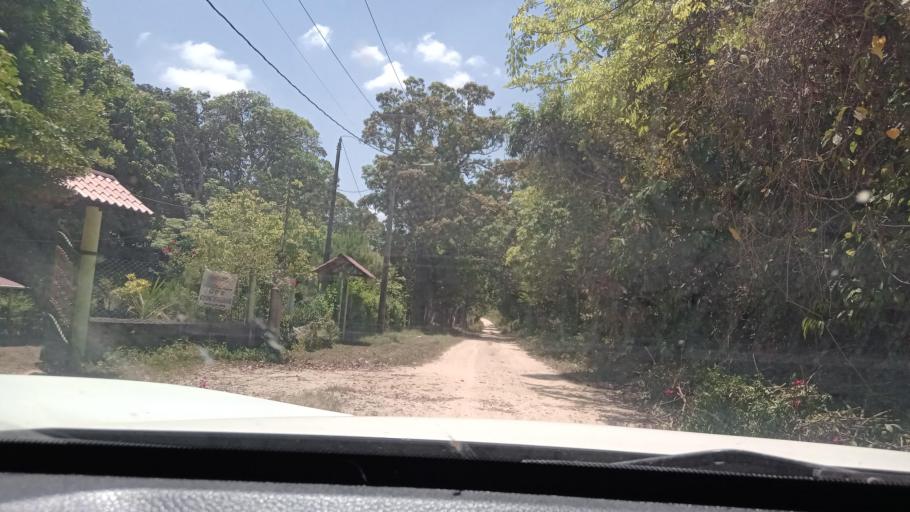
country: MX
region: Veracruz
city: Las Choapas
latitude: 17.7530
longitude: -94.1088
